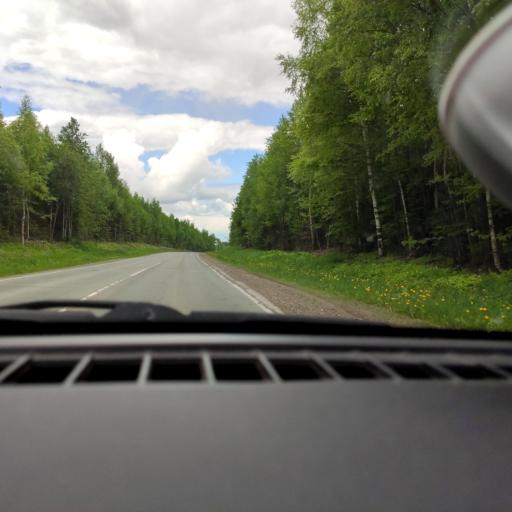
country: RU
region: Perm
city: Perm
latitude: 58.2227
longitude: 56.1656
